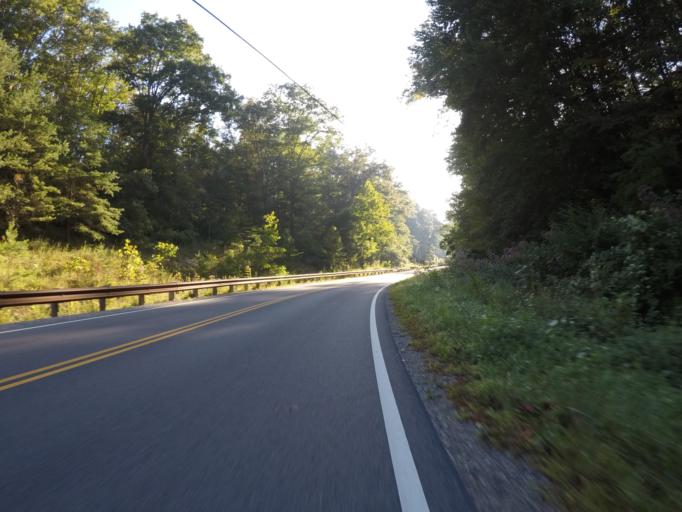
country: US
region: Ohio
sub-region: Lawrence County
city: Ironton
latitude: 38.6132
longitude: -82.6016
